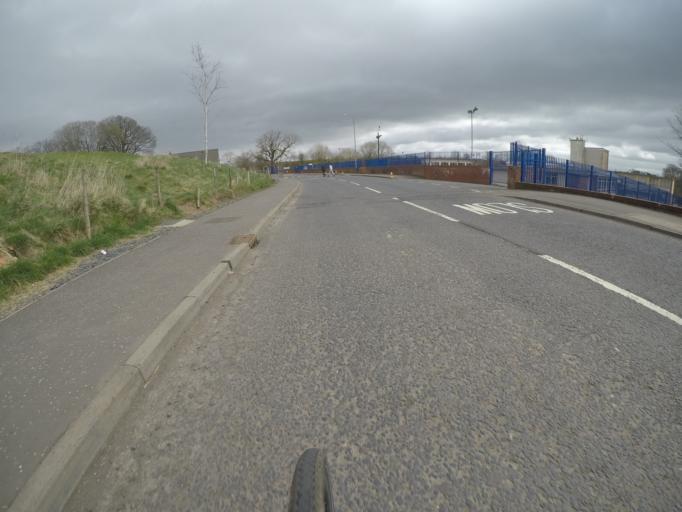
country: GB
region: Scotland
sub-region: East Ayrshire
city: Stewarton
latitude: 55.6792
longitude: -4.5222
